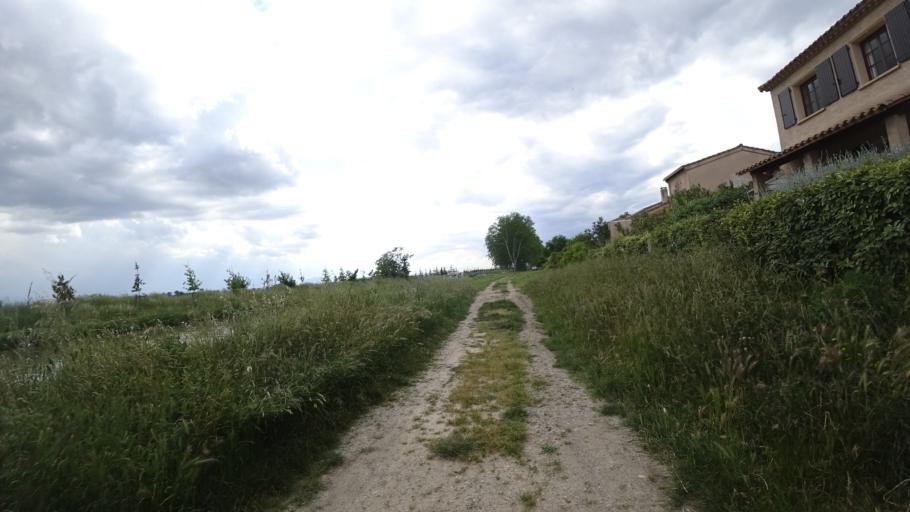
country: FR
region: Languedoc-Roussillon
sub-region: Departement de l'Aude
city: Canet
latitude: 43.2482
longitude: 2.8528
